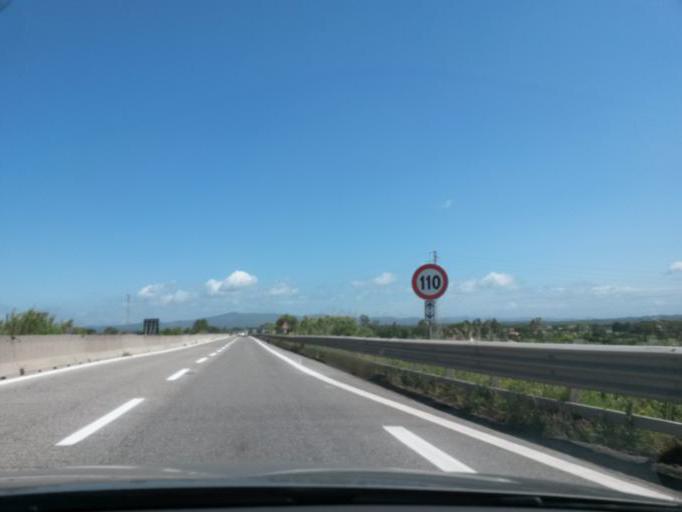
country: IT
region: Tuscany
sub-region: Provincia di Livorno
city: La California
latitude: 43.2806
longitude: 10.5409
